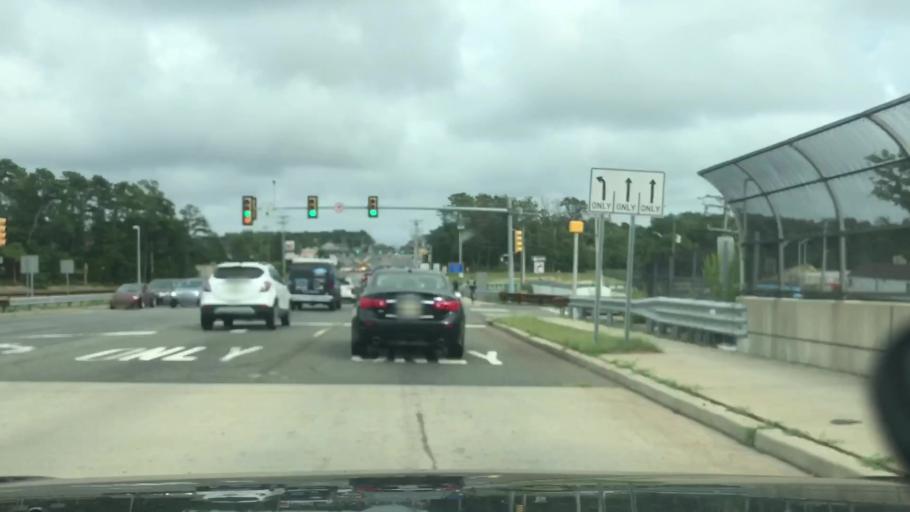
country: US
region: New Jersey
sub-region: Ocean County
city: Barnegat
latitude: 39.7590
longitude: -74.2496
